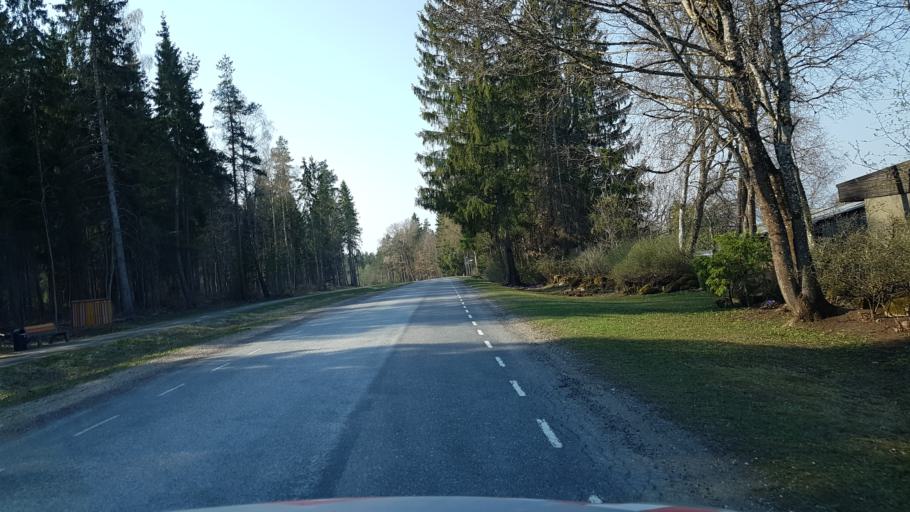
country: EE
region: Raplamaa
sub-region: Kohila vald
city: Kohila
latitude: 59.1733
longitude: 24.6555
